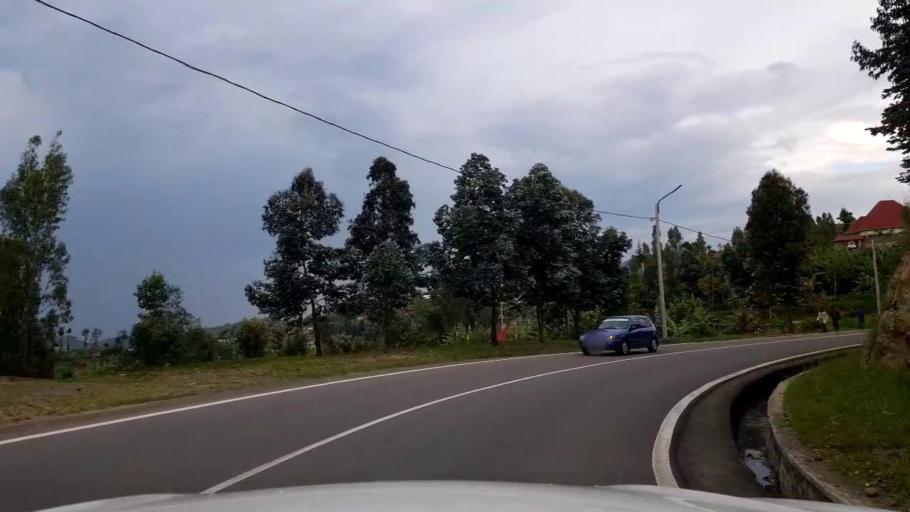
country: RW
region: Western Province
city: Kibuye
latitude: -2.0458
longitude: 29.4086
